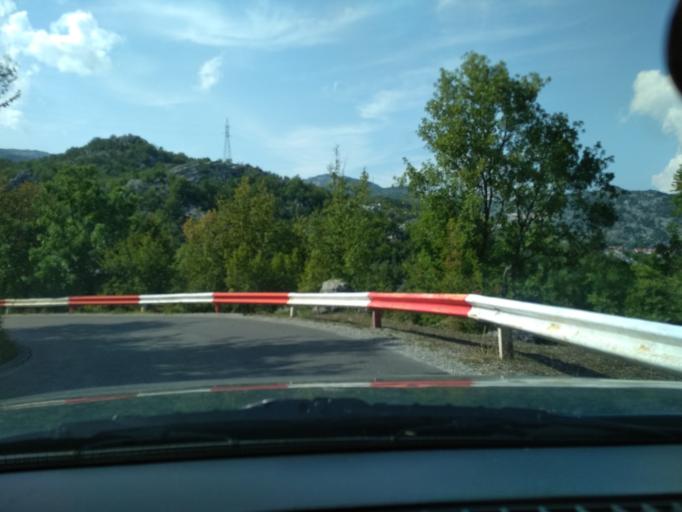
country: ME
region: Cetinje
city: Cetinje
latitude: 42.3898
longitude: 18.9035
